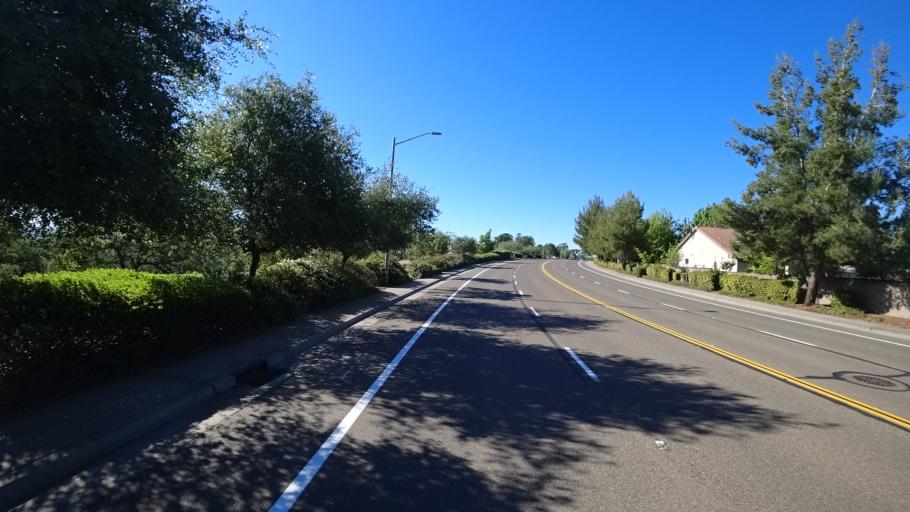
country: US
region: California
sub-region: Placer County
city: Loomis
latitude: 38.8355
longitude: -121.2294
